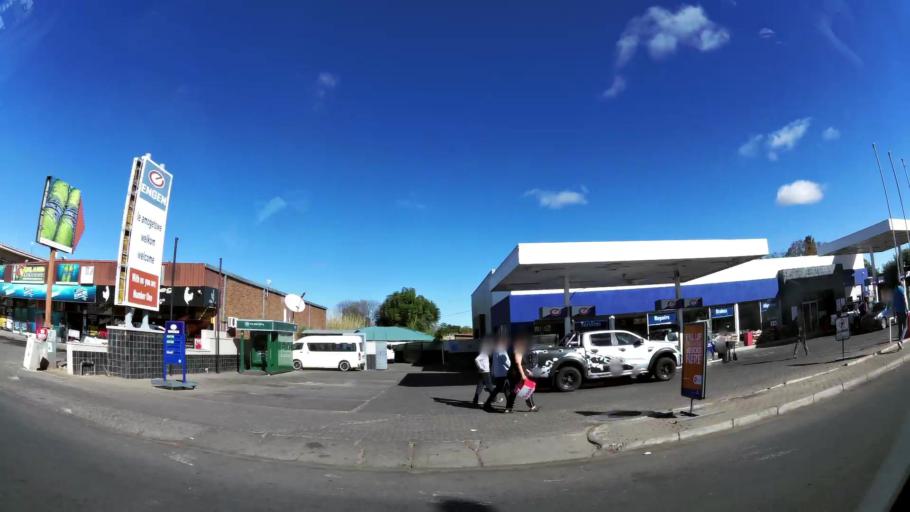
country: ZA
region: Limpopo
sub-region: Capricorn District Municipality
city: Polokwane
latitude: -23.8797
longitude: 29.4420
